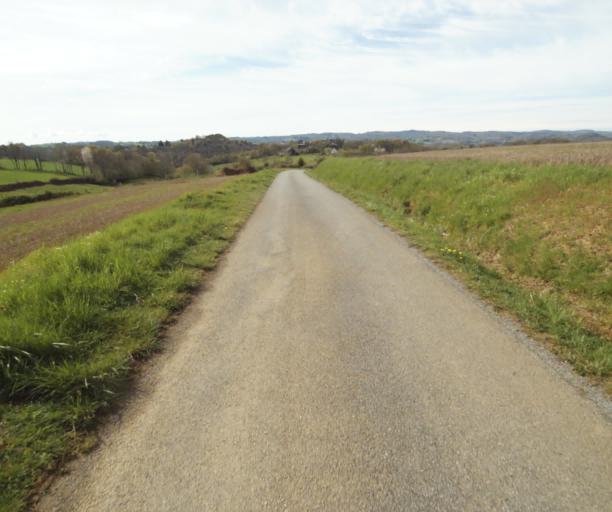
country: FR
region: Limousin
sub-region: Departement de la Correze
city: Laguenne
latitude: 45.2675
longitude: 1.8082
